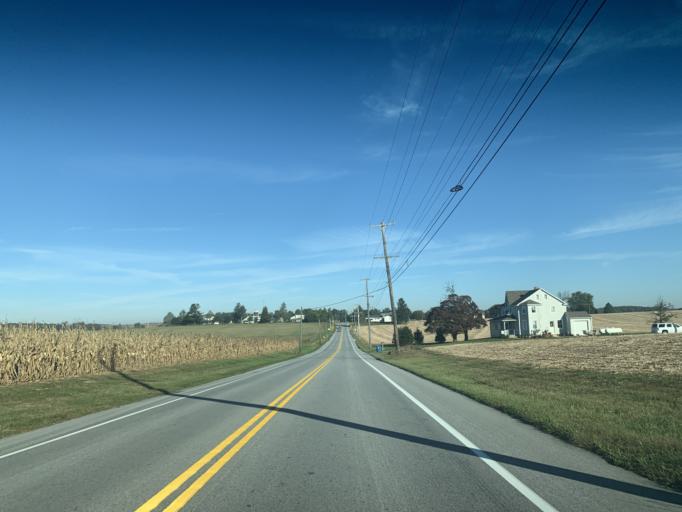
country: US
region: Pennsylvania
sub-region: Chester County
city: Parkesburg
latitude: 39.9139
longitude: -75.9111
